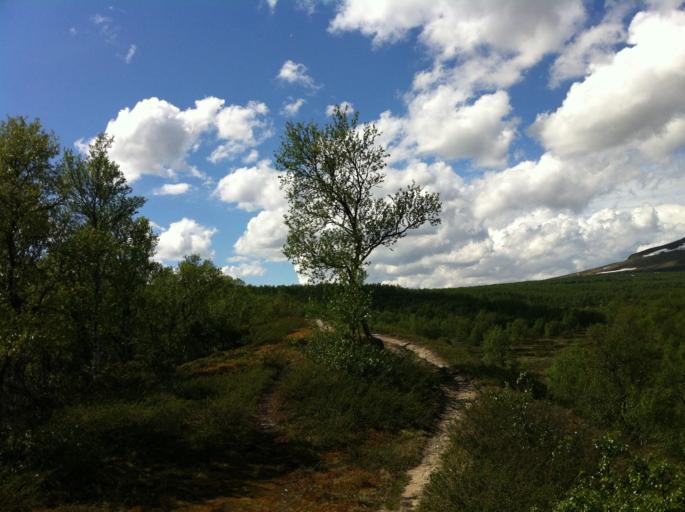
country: SE
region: Jaemtland
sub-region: Are Kommun
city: Are
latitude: 62.7099
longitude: 12.4975
